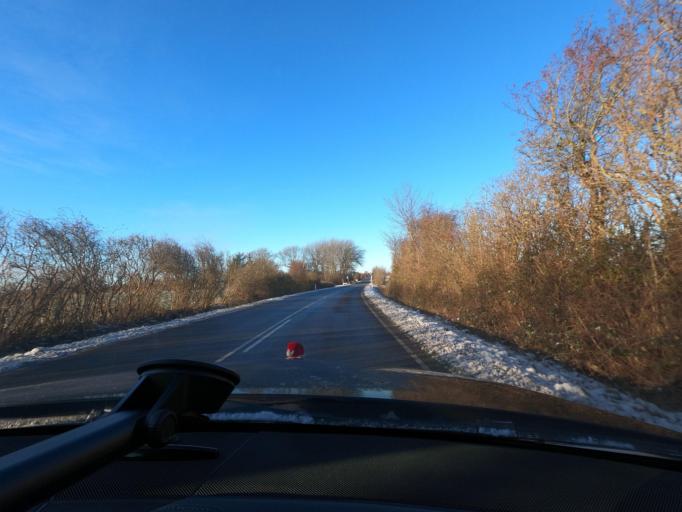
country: DK
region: South Denmark
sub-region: Sonderborg Kommune
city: Horuphav
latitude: 54.8576
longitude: 9.9768
